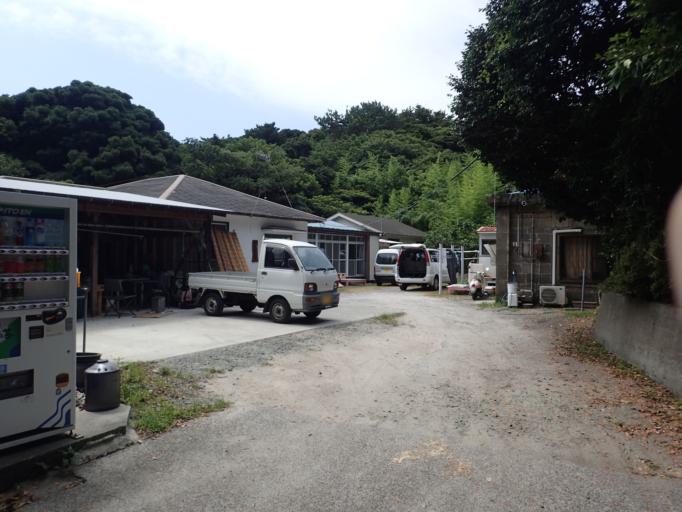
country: JP
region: Shizuoka
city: Shimoda
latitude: 34.3290
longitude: 139.2237
